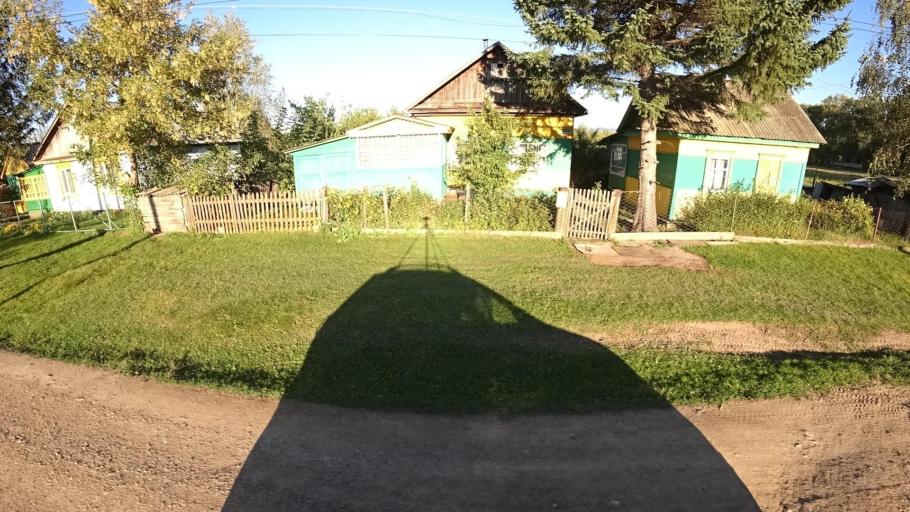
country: RU
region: Primorskiy
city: Kirovskiy
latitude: 44.8319
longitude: 133.5754
